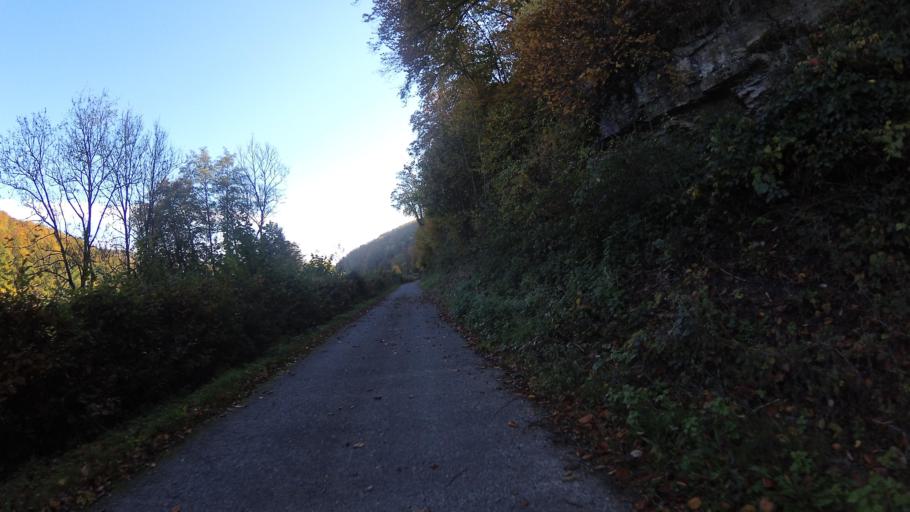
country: DE
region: Baden-Wuerttemberg
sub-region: Regierungsbezirk Stuttgart
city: Jagsthausen
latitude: 49.2685
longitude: 9.4476
